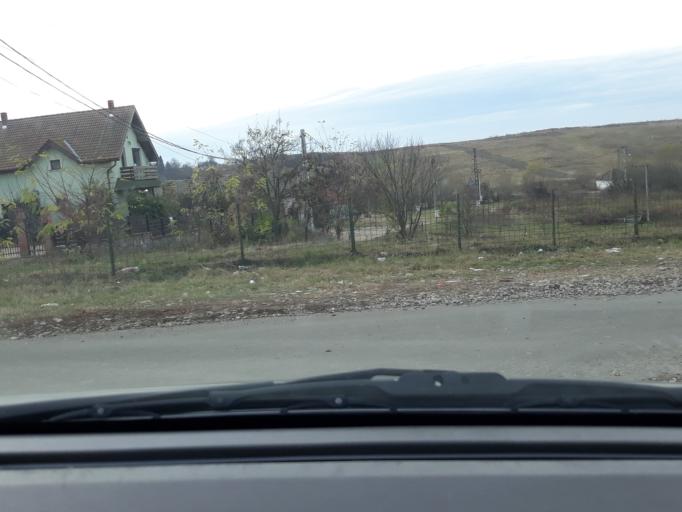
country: RO
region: Bihor
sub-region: Comuna Osorheiu
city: Alparea
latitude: 47.0125
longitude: 22.0205
